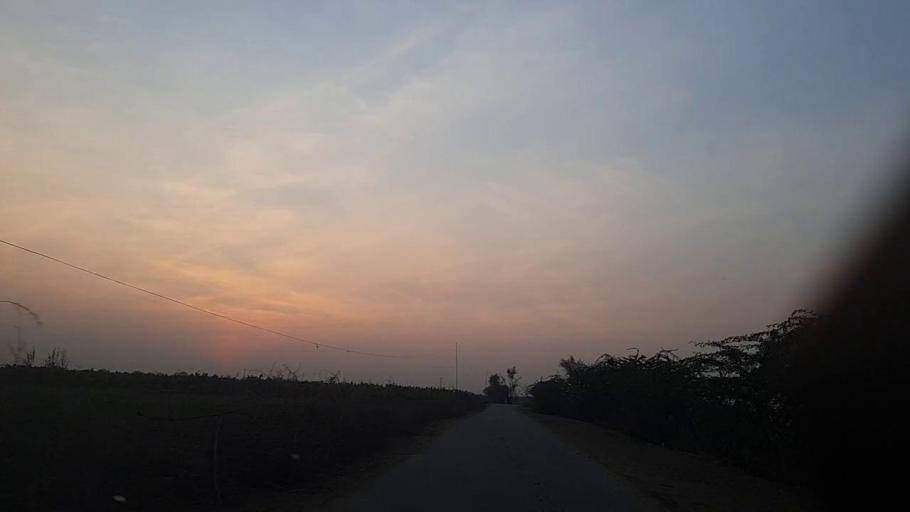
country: PK
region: Sindh
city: Sakrand
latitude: 26.0963
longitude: 68.3422
